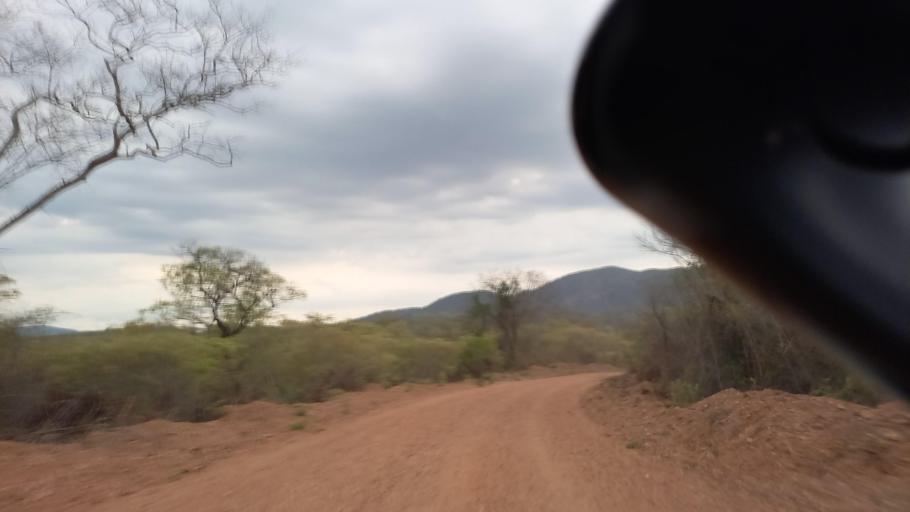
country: ZW
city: Chirundu
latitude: -16.0514
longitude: 28.4842
